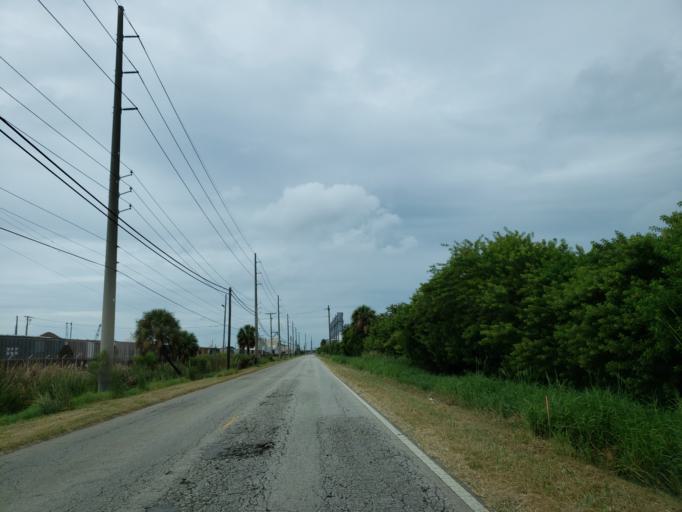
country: US
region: Florida
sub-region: Hillsborough County
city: Palm River-Clair Mel
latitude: 27.9063
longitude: -82.4102
